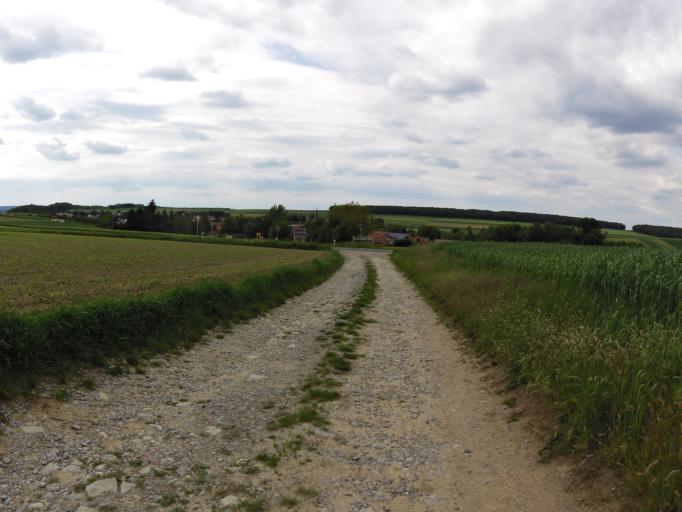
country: DE
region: Bavaria
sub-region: Regierungsbezirk Unterfranken
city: Theilheim
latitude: 49.7303
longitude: 10.0398
